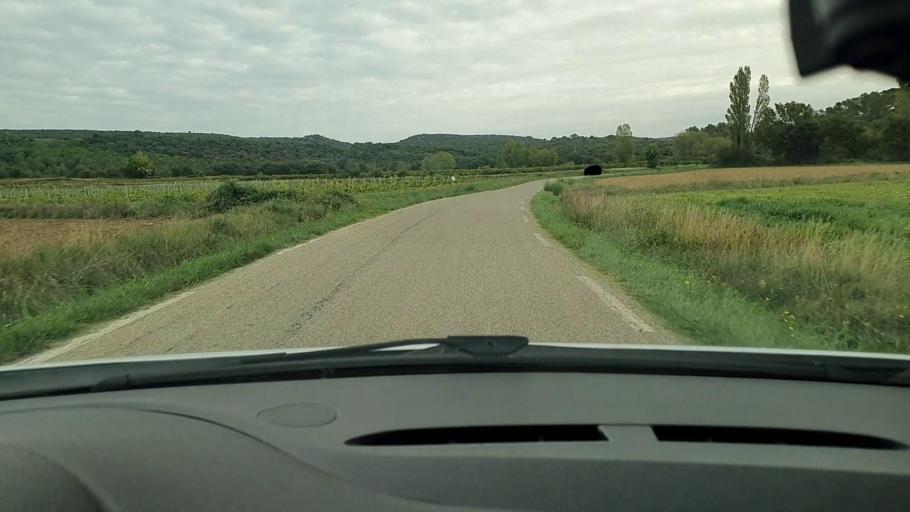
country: FR
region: Languedoc-Roussillon
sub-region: Departement du Gard
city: Montaren-et-Saint-Mediers
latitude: 44.0471
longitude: 4.3097
